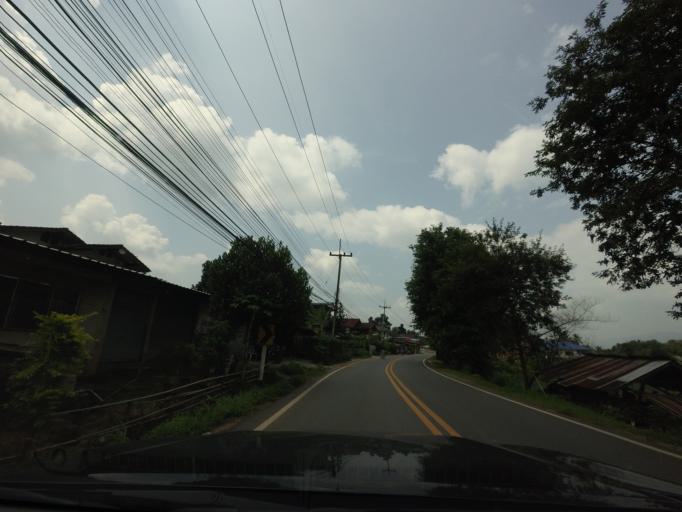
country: TH
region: Nan
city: Pua
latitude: 19.1541
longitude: 100.9328
